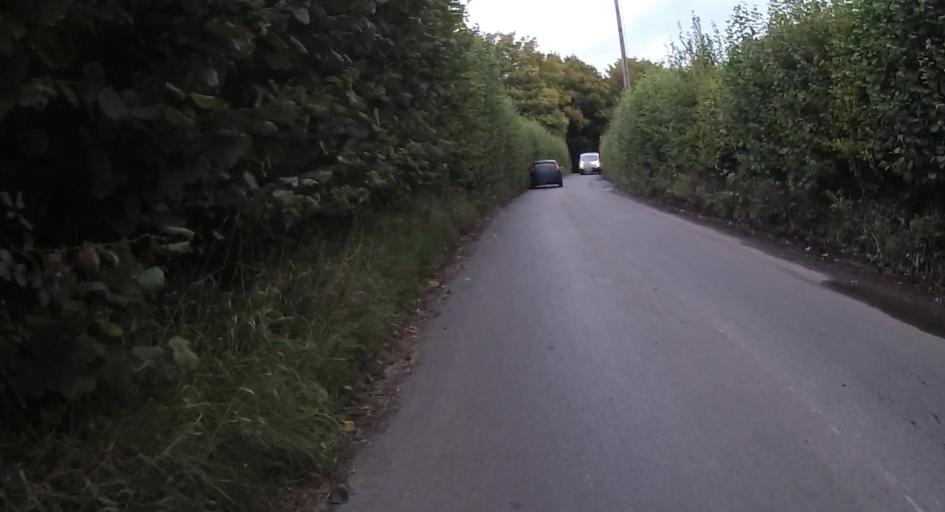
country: GB
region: England
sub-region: Hampshire
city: Alton
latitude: 51.1265
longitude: -0.9447
